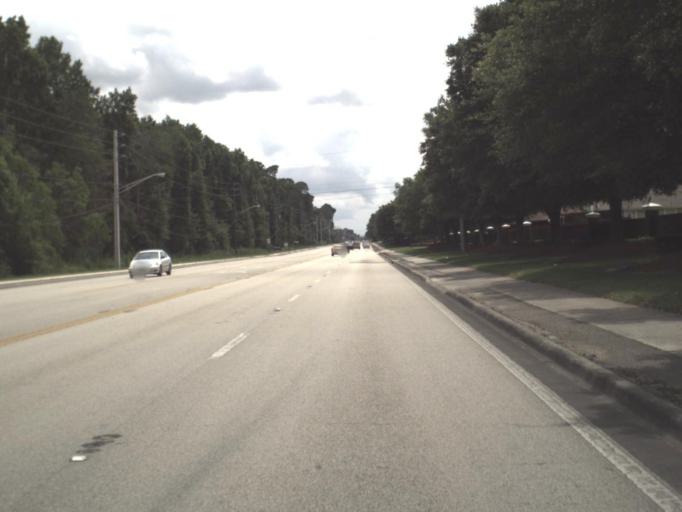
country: US
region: Florida
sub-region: Duval County
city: Jacksonville
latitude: 30.4385
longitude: -81.7095
